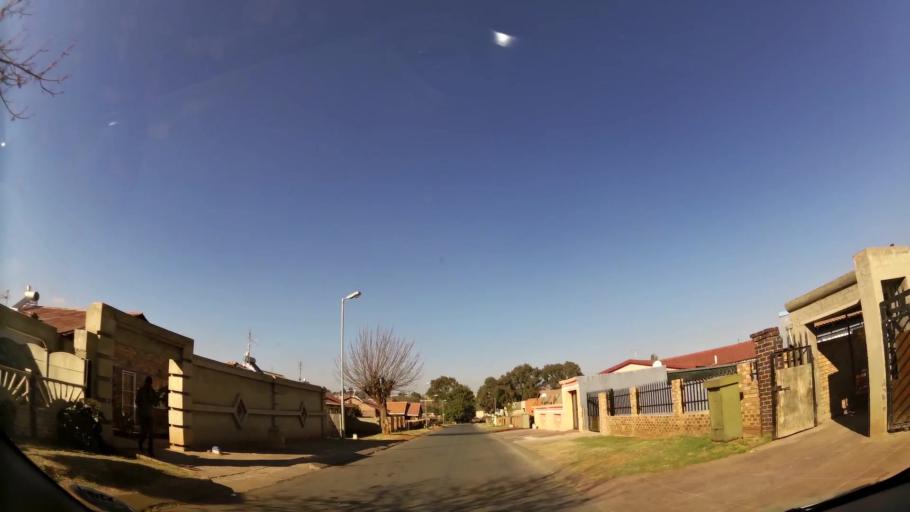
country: ZA
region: Gauteng
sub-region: City of Johannesburg Metropolitan Municipality
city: Roodepoort
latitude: -26.1569
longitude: 27.8486
